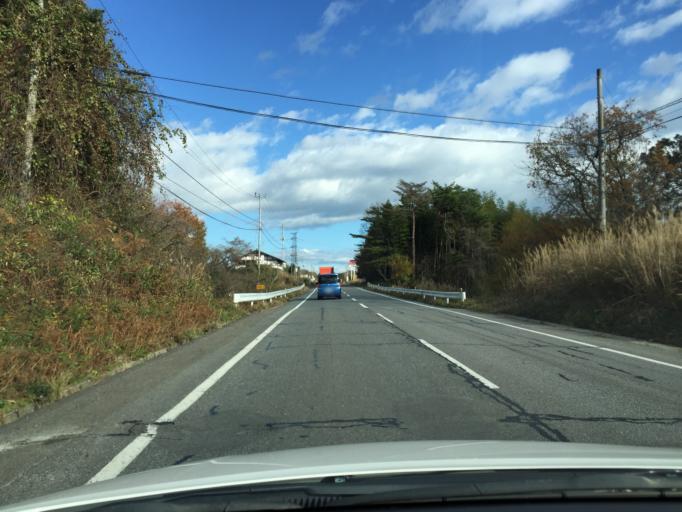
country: JP
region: Fukushima
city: Namie
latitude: 37.4195
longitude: 141.0015
